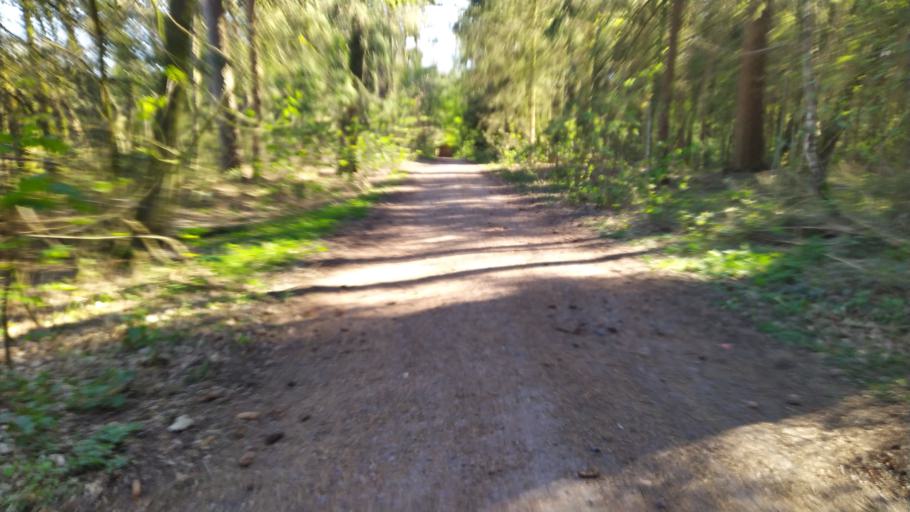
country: DE
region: Lower Saxony
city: Klein Meckelsen
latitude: 53.2968
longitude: 9.4365
